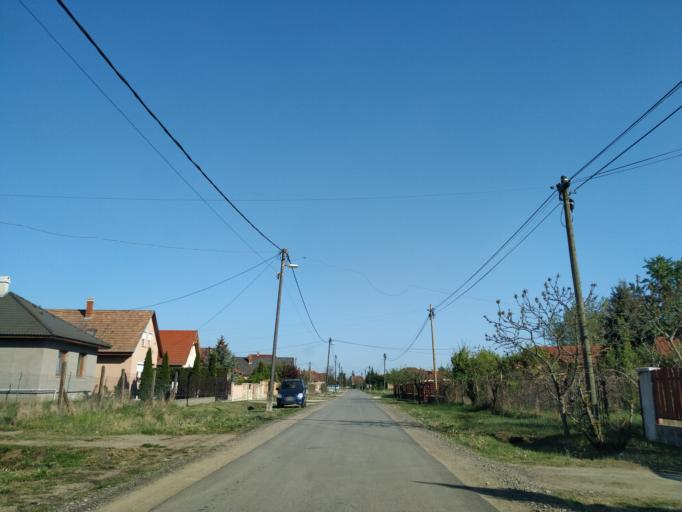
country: HU
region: Pest
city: Nagykata
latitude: 47.4220
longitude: 19.7241
